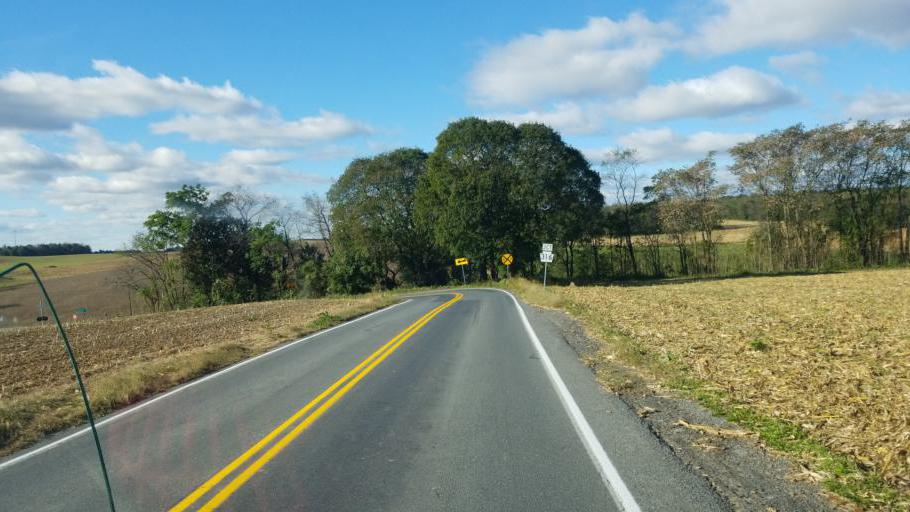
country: US
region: Pennsylvania
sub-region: Franklin County
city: Guilford Siding
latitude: 39.8493
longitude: -77.6087
